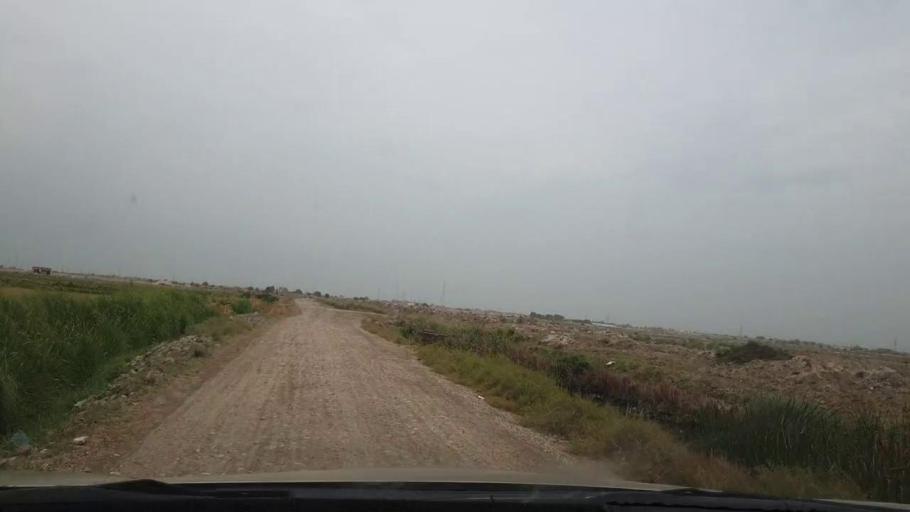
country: PK
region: Sindh
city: Ratodero
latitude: 27.7763
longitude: 68.2786
